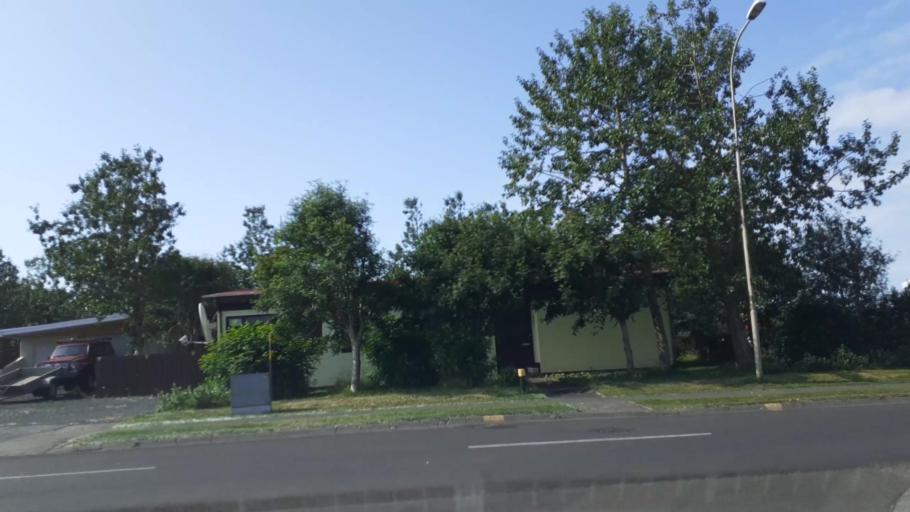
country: IS
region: Northwest
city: Saudarkrokur
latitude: 65.6635
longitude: -20.2895
